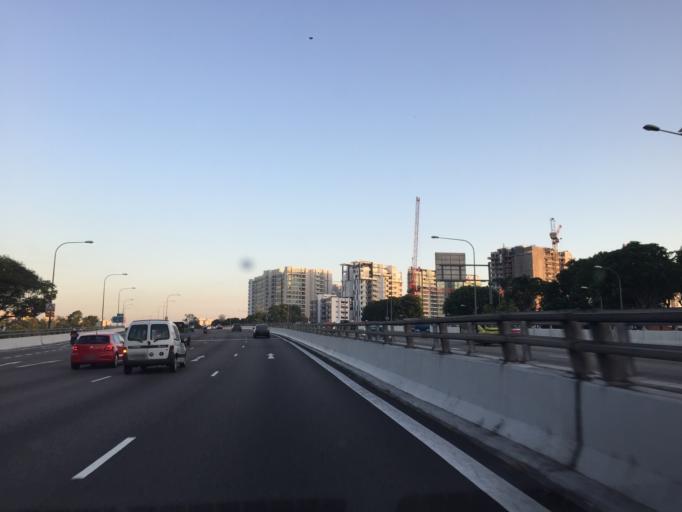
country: SG
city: Singapore
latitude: 1.3265
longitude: 103.8704
